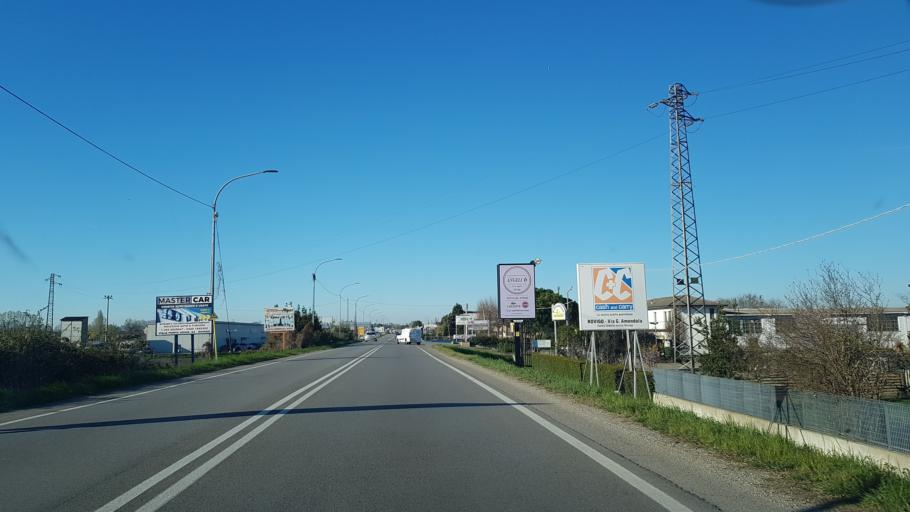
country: IT
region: Veneto
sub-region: Provincia di Padova
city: Boara Pisani
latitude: 45.0914
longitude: 11.7855
